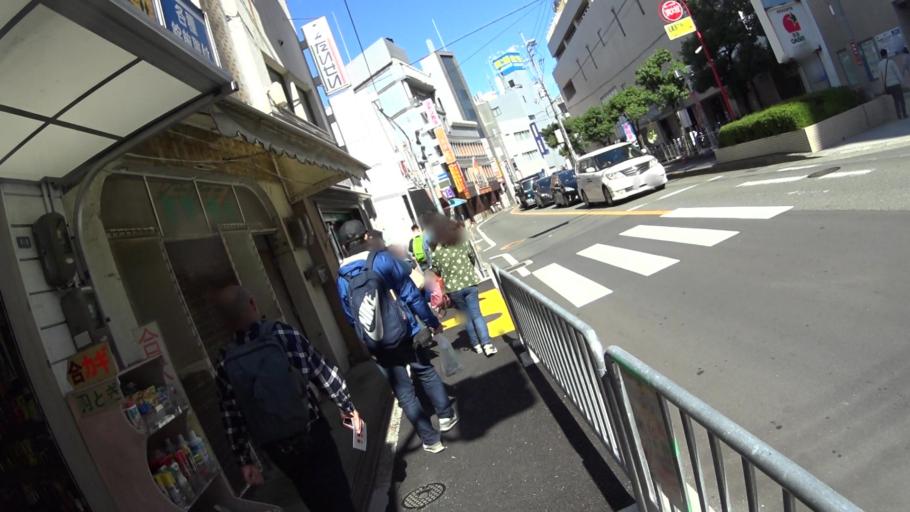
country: JP
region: Osaka
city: Ikeda
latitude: 34.8210
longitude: 135.4245
